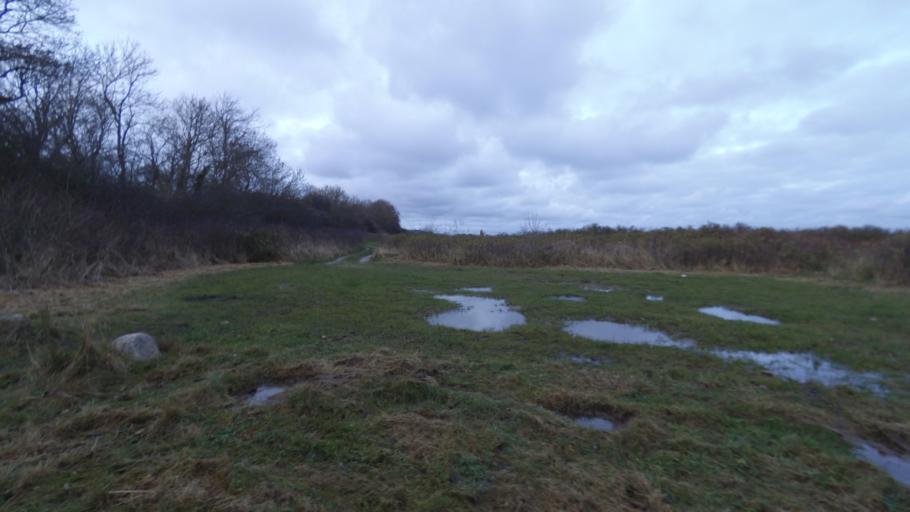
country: DK
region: Central Jutland
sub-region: Arhus Kommune
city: Beder
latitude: 56.0494
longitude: 10.2692
